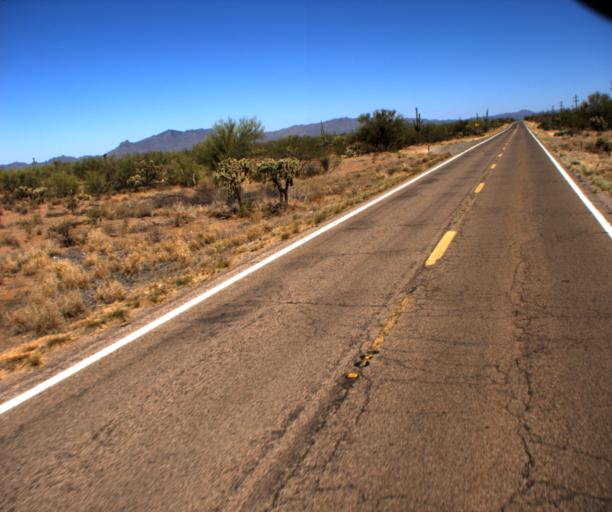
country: US
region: Arizona
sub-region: Pima County
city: Sells
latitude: 32.0026
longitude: -111.9873
